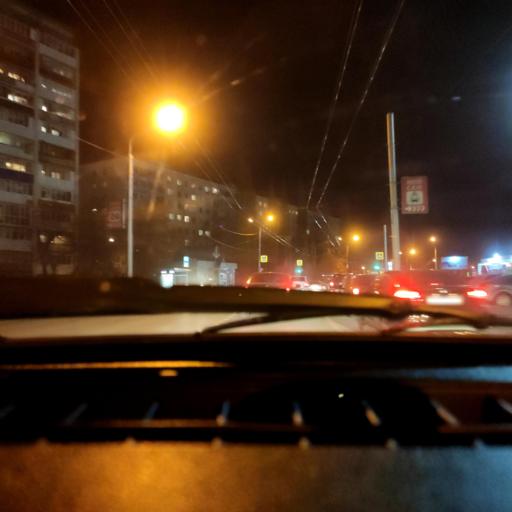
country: RU
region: Bashkortostan
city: Ufa
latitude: 54.7856
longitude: 56.1239
